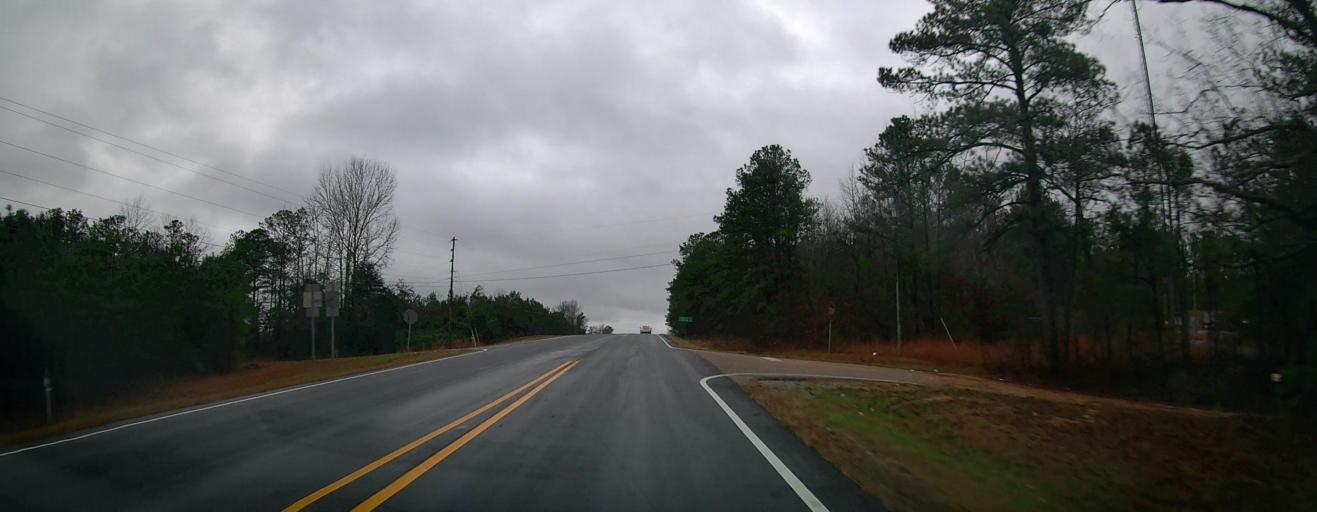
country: US
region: Alabama
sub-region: Bibb County
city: Centreville
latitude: 32.8145
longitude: -86.9334
